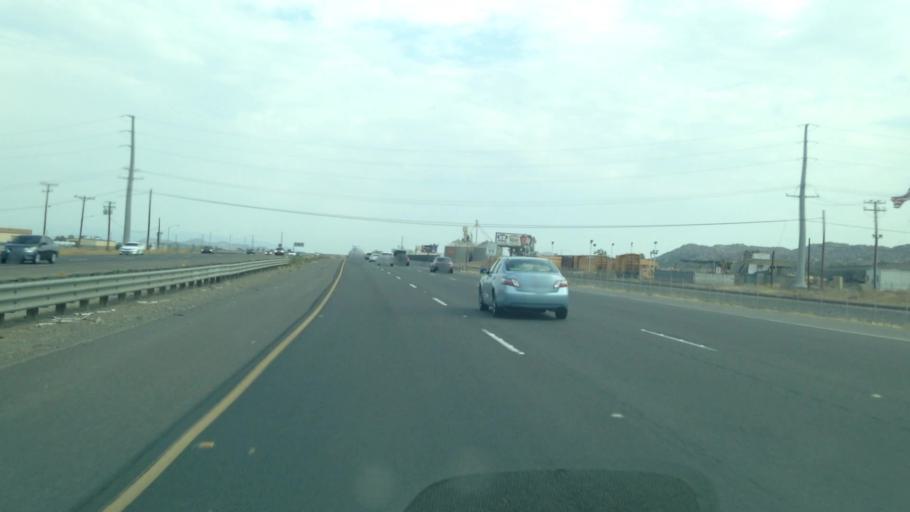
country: US
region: California
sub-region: Riverside County
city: Mead Valley
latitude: 33.8391
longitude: -117.2495
